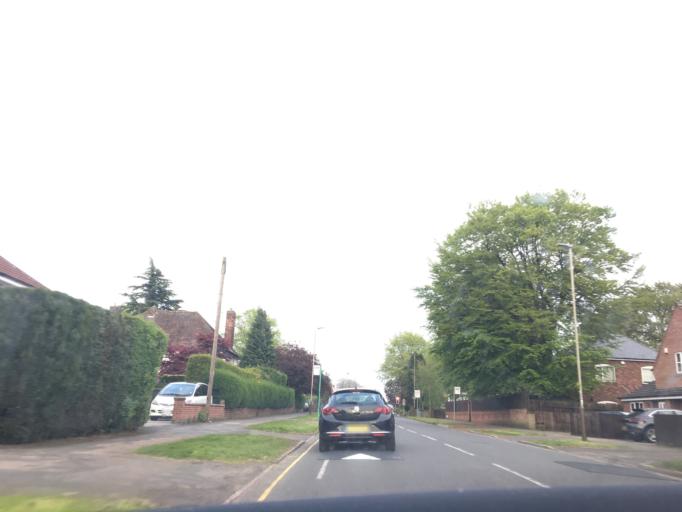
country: GB
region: England
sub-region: Leicestershire
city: Oadby
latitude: 52.6263
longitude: -1.0696
